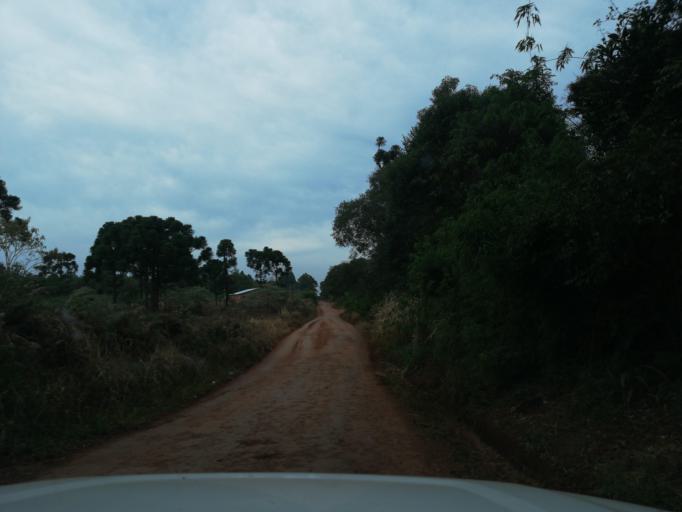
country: AR
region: Misiones
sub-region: Departamento de San Pedro
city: San Pedro
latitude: -26.6334
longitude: -54.0991
